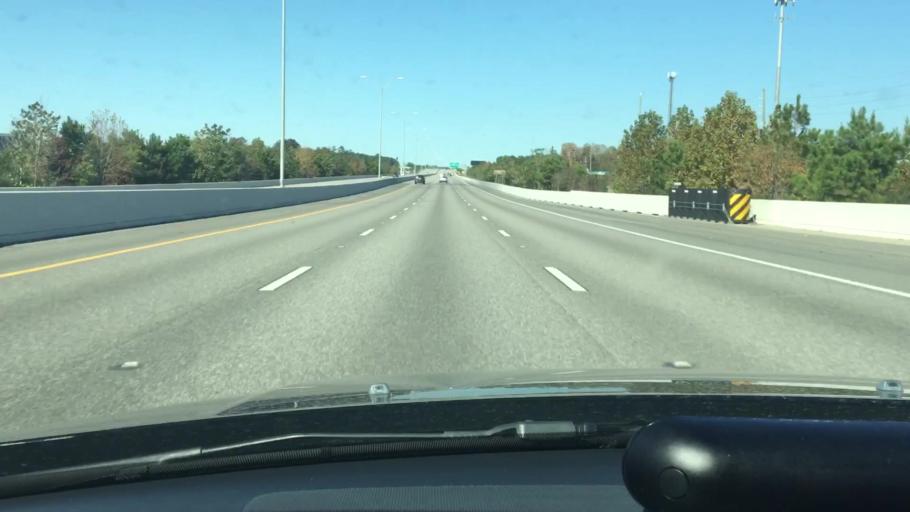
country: US
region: Texas
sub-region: Harris County
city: Sheldon
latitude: 29.8735
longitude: -95.1893
